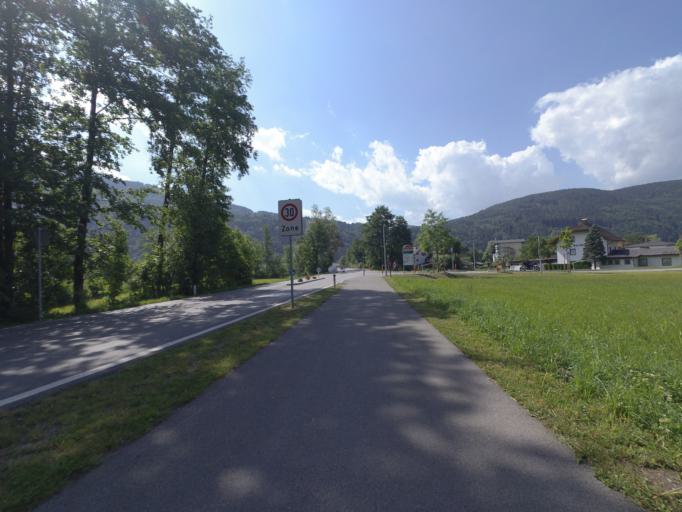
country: AT
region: Carinthia
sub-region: Politischer Bezirk Villach Land
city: Ferndorf
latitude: 46.7746
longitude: 13.6446
